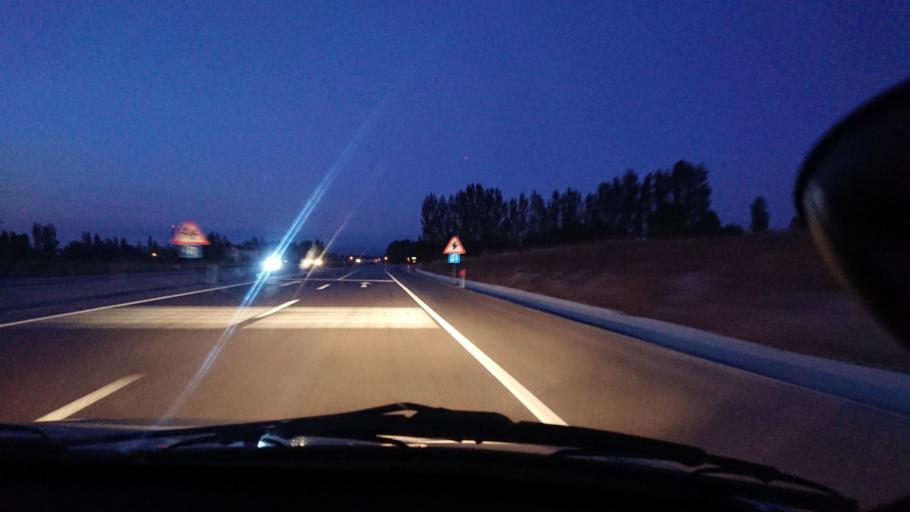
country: TR
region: Kuetahya
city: Cavdarhisar
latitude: 39.1869
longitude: 29.6195
